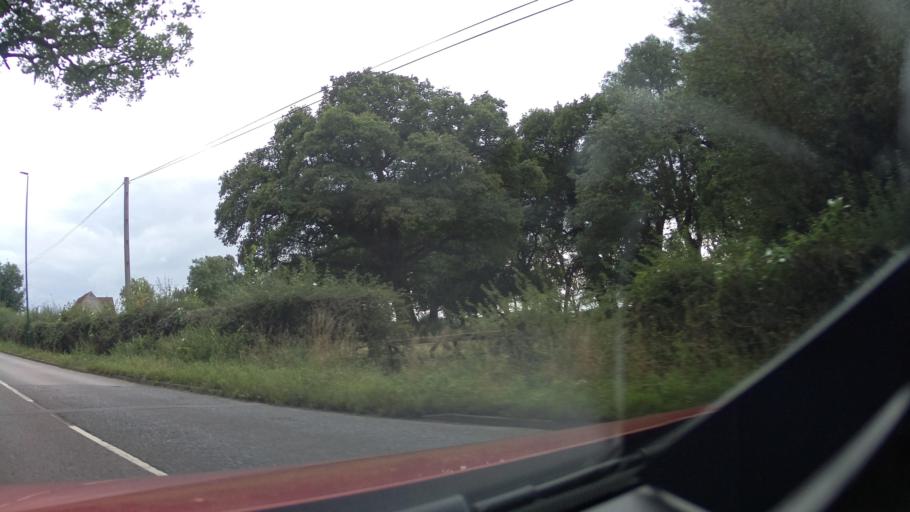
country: GB
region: England
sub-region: Solihull
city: Cheswick Green
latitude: 52.3687
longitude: -1.7844
